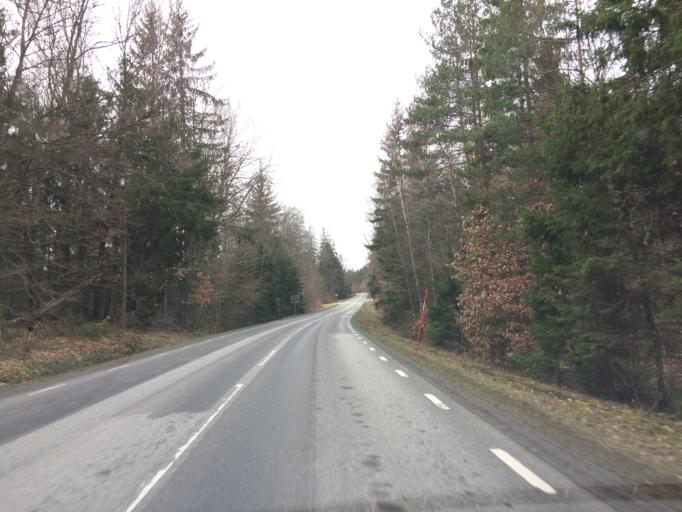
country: SE
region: Skane
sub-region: Ostra Goinge Kommun
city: Sibbhult
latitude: 56.2878
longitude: 14.2892
